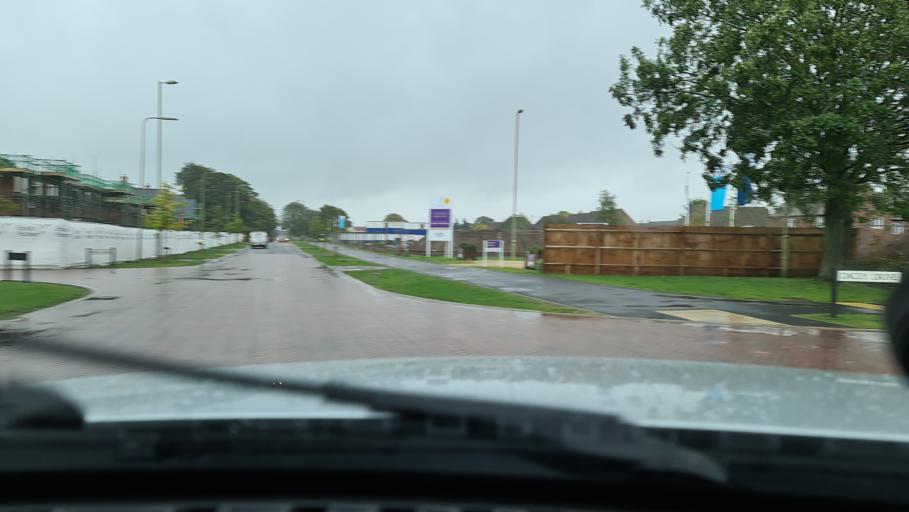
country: GB
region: England
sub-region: Oxfordshire
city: Somerton
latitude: 51.9288
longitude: -1.2610
